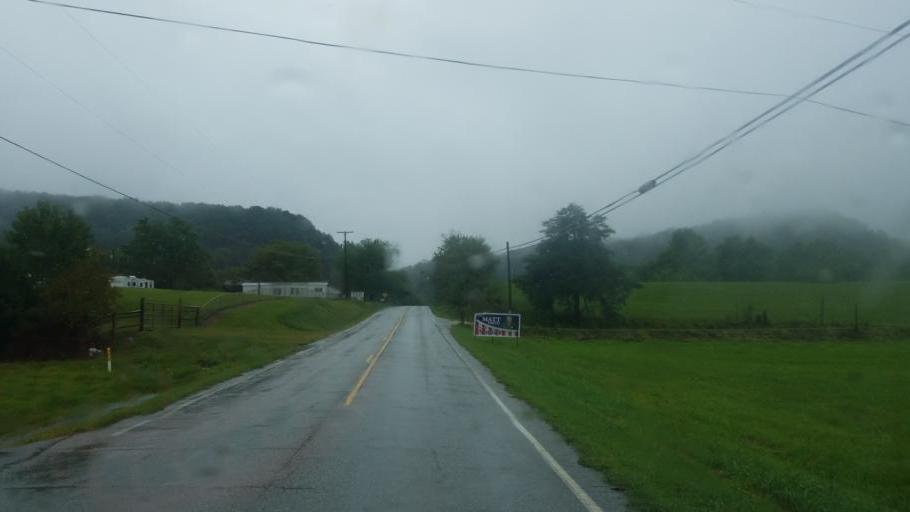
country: US
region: Kentucky
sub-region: Greenup County
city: South Shore
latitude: 38.7041
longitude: -82.9463
